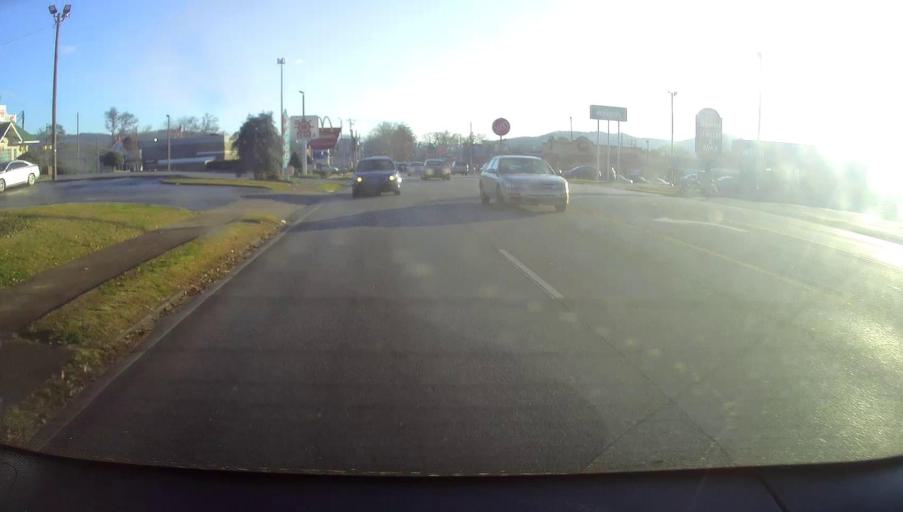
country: US
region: Alabama
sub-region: Calhoun County
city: Anniston
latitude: 33.6701
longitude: -85.8267
